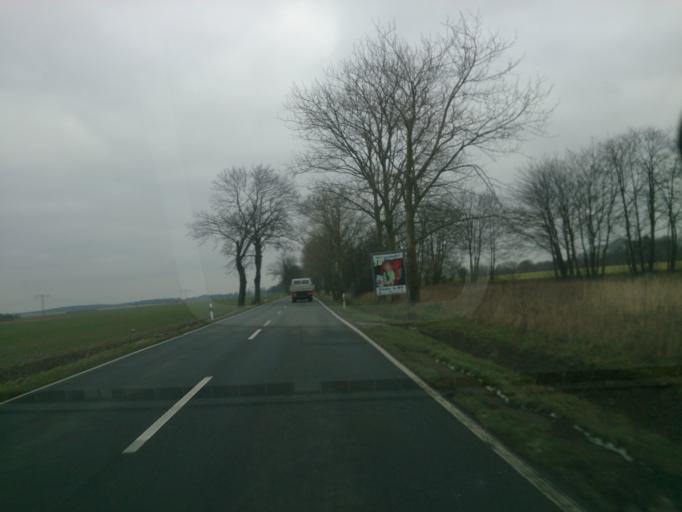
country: DE
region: Mecklenburg-Vorpommern
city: Borrentin
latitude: 53.8276
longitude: 12.9843
